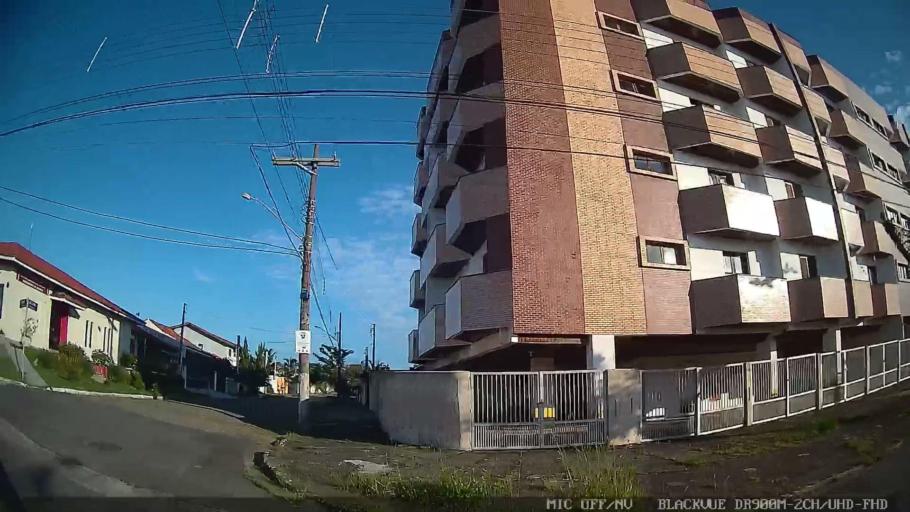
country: BR
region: Sao Paulo
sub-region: Peruibe
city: Peruibe
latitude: -24.2926
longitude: -46.9645
